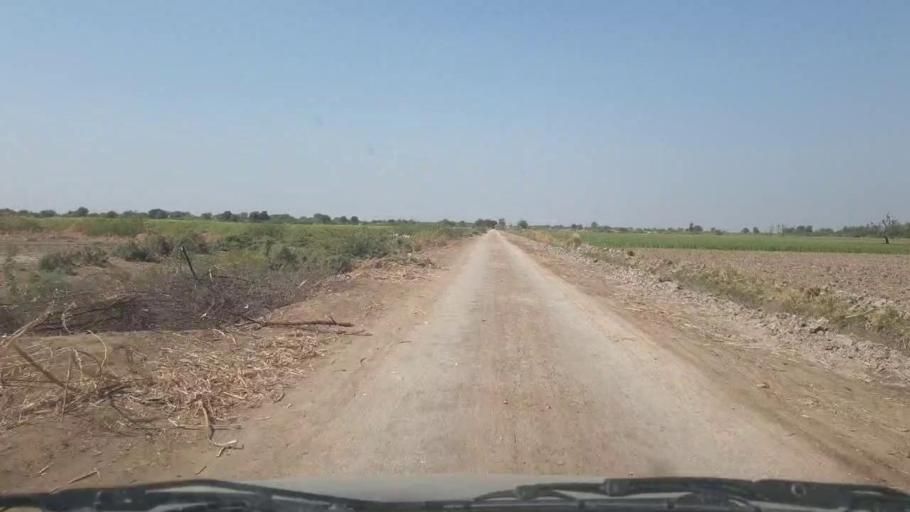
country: PK
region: Sindh
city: Samaro
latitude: 25.2237
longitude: 69.3296
